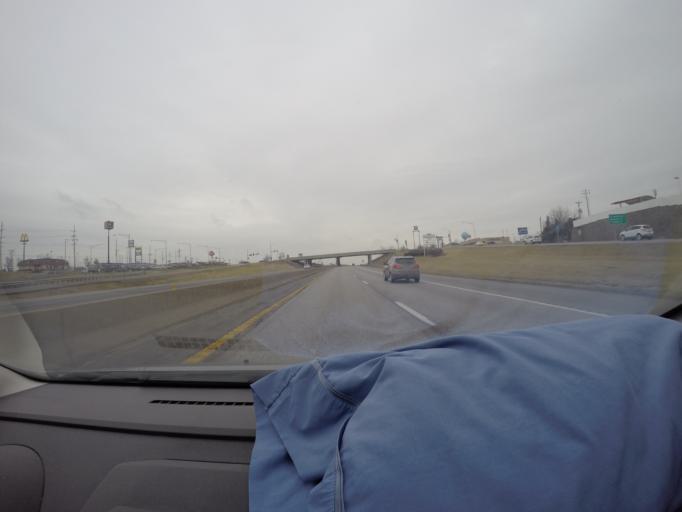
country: US
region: Missouri
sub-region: Warren County
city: Warrenton
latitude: 38.8215
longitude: -91.1412
